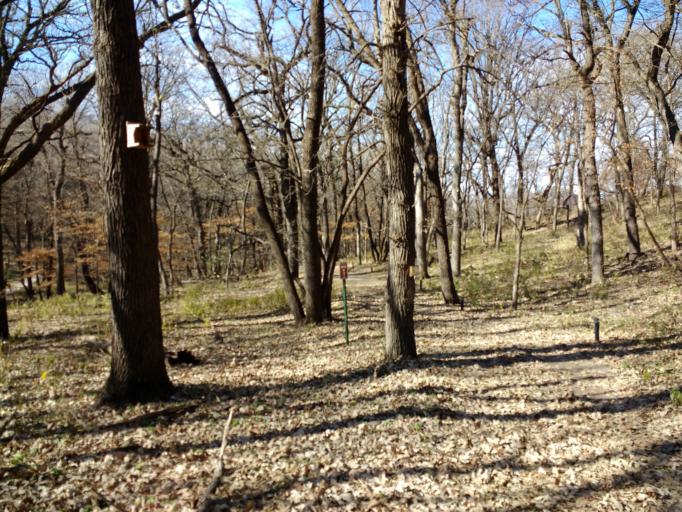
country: US
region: South Dakota
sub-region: Union County
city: North Sioux City
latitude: 42.5422
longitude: -96.4702
